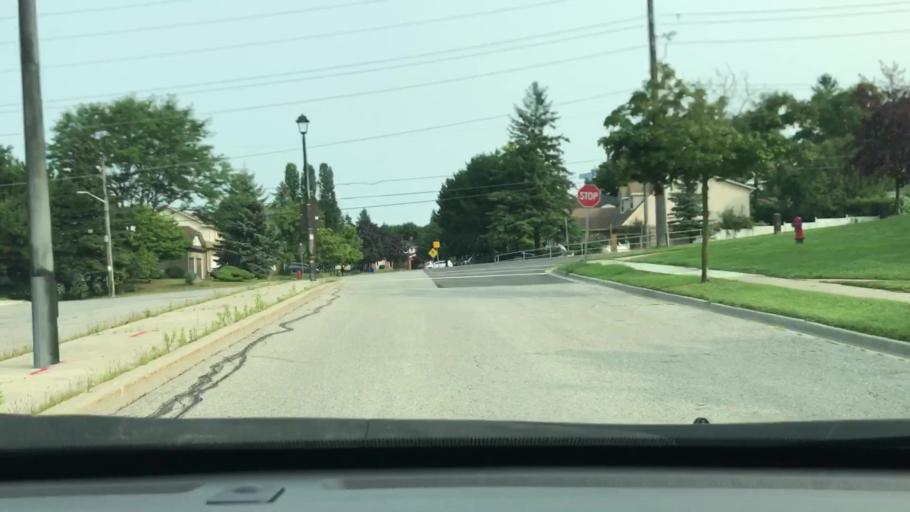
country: CA
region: Ontario
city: Newmarket
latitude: 44.0558
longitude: -79.4321
